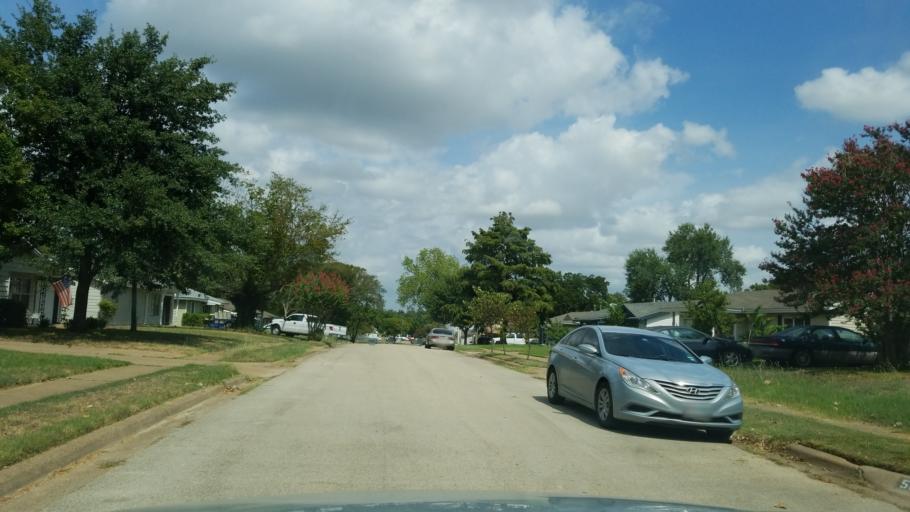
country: US
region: Texas
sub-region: Tarrant County
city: Euless
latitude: 32.8428
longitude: -97.0872
